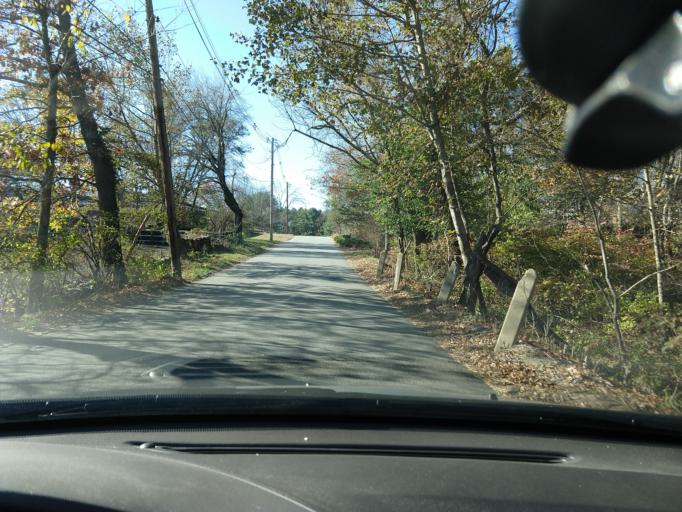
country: US
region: Massachusetts
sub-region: Middlesex County
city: Carlisle
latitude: 42.5095
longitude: -71.3225
